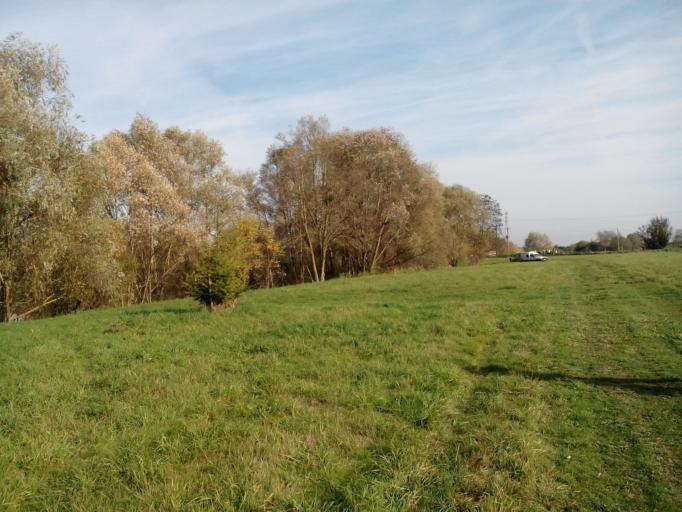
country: FR
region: Centre
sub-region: Departement d'Indre-et-Loire
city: Fondettes
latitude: 47.3804
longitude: 0.6130
